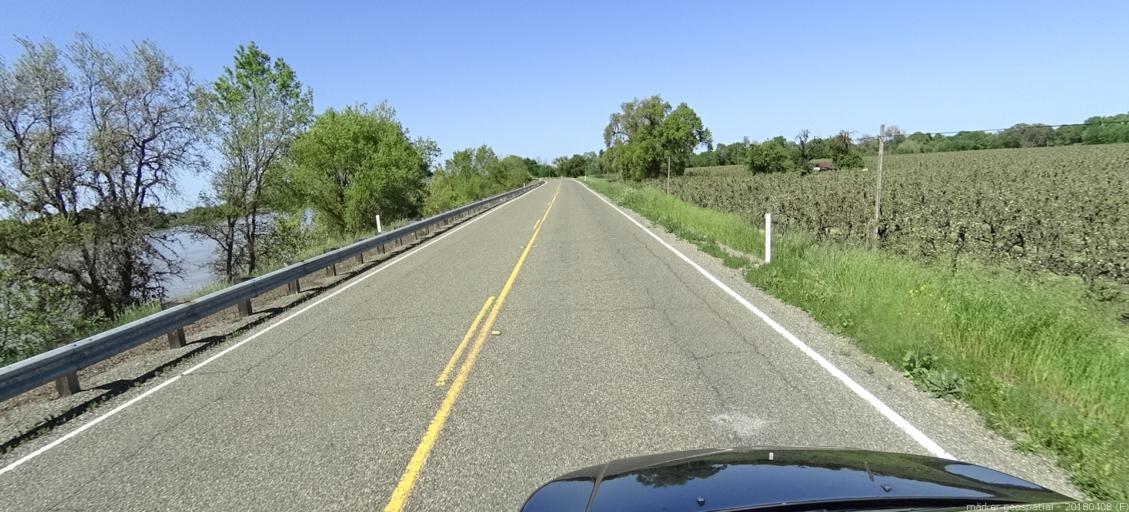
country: US
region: California
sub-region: Sacramento County
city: Laguna
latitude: 38.3952
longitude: -121.5119
